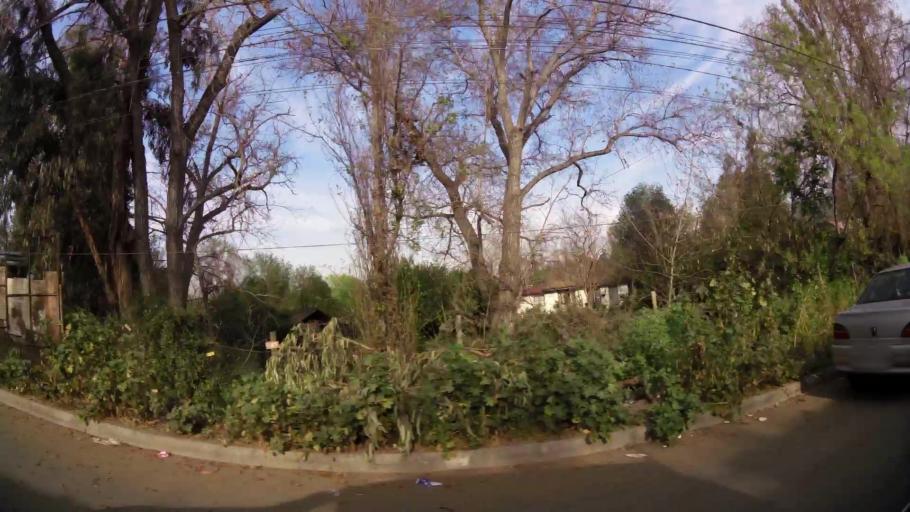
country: CL
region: Santiago Metropolitan
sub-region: Provincia de Talagante
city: Talagante
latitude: -33.6625
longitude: -70.9343
